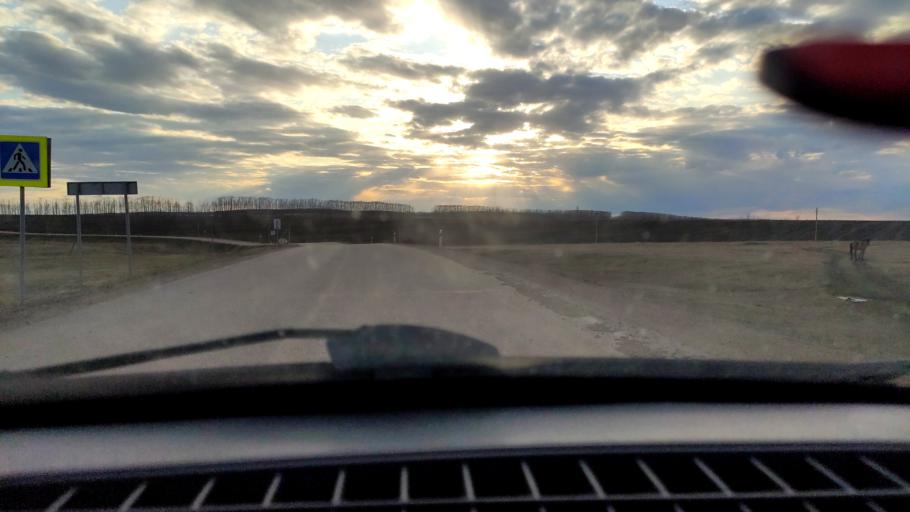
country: RU
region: Bashkortostan
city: Tolbazy
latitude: 53.9884
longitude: 55.8078
